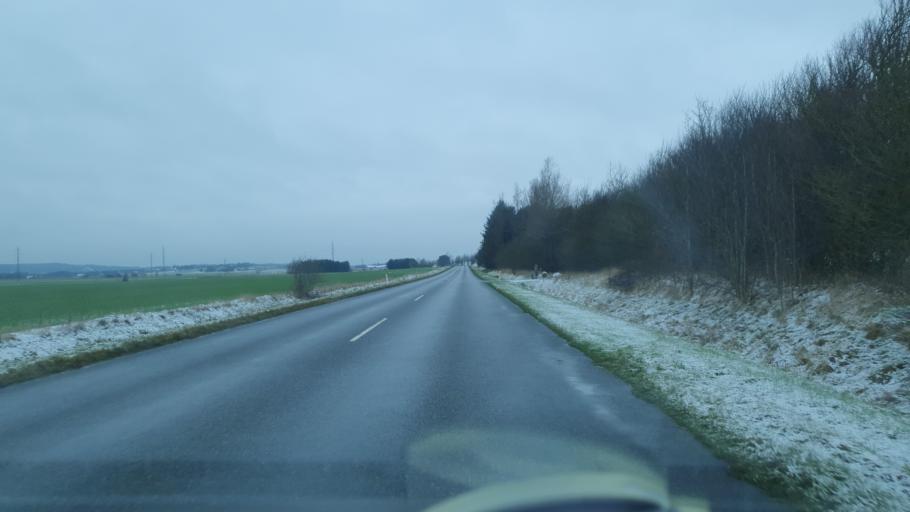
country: DK
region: North Denmark
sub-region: Jammerbugt Kommune
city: Brovst
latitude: 57.1065
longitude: 9.5020
